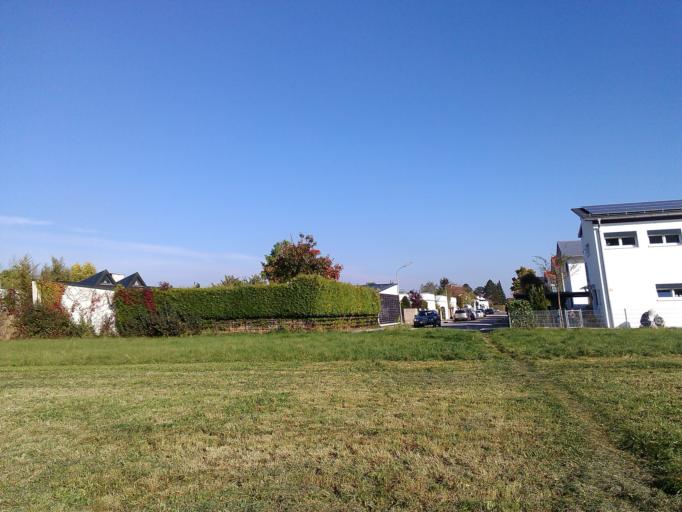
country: DE
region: Bavaria
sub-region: Upper Bavaria
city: Gauting
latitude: 48.0658
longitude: 11.3665
